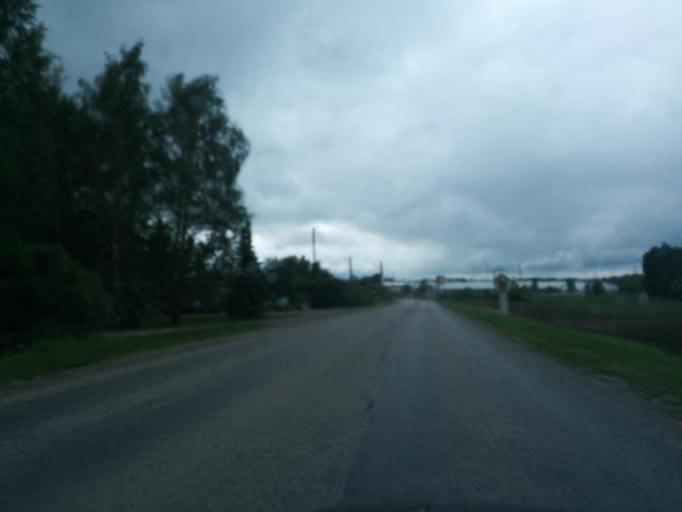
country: LV
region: Valmieras Rajons
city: Valmiera
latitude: 57.5168
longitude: 25.4554
